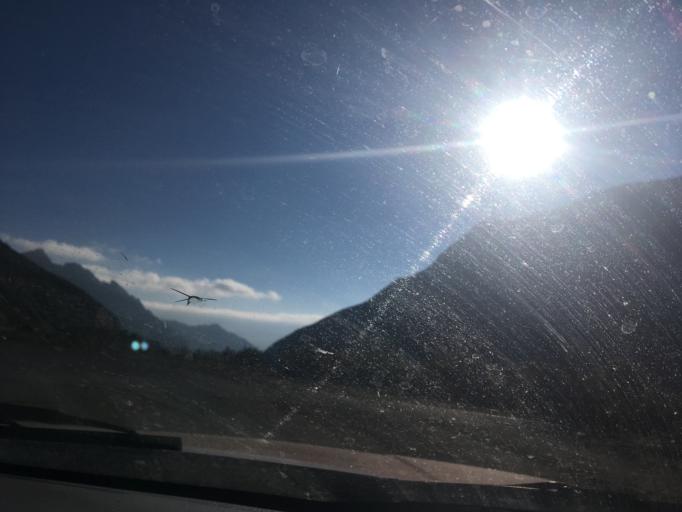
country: BO
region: La Paz
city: Quime
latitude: -17.0156
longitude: -67.2781
